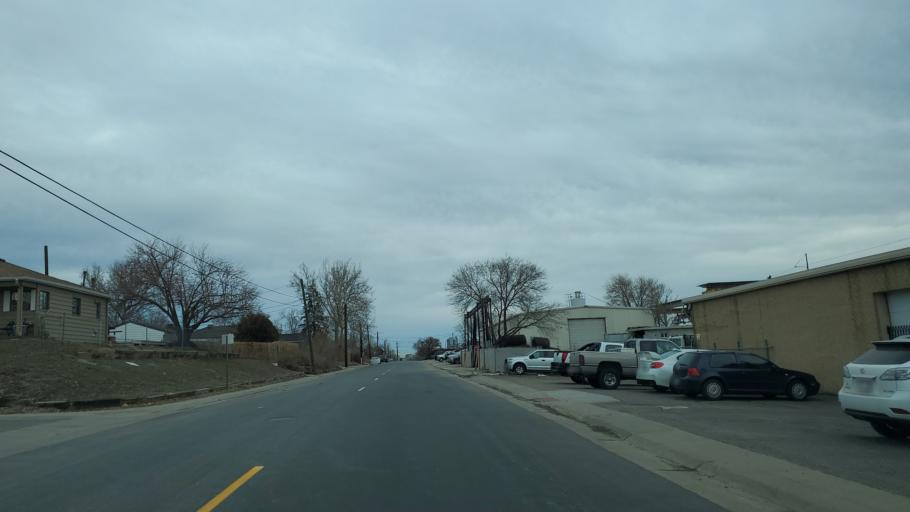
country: US
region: Colorado
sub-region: Denver County
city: Denver
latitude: 39.6979
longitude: -105.0015
